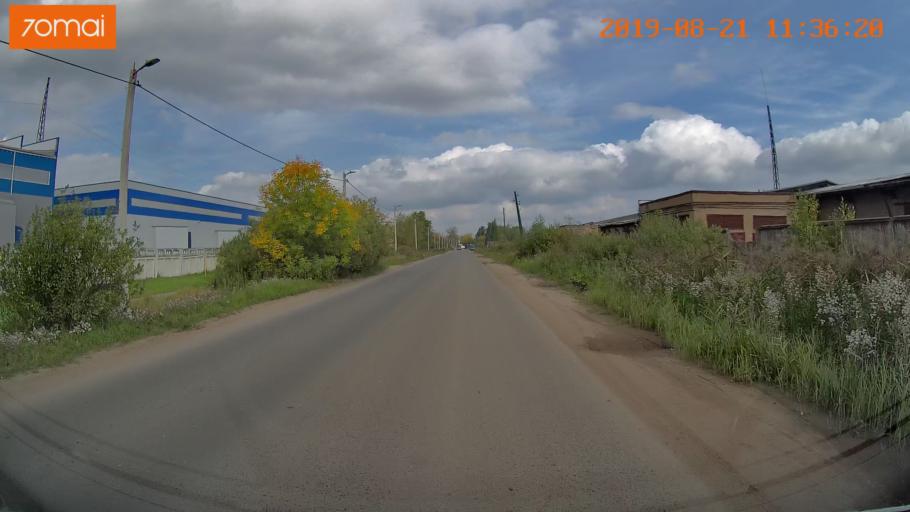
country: RU
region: Ivanovo
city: Novo-Talitsy
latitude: 56.9925
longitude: 40.9102
